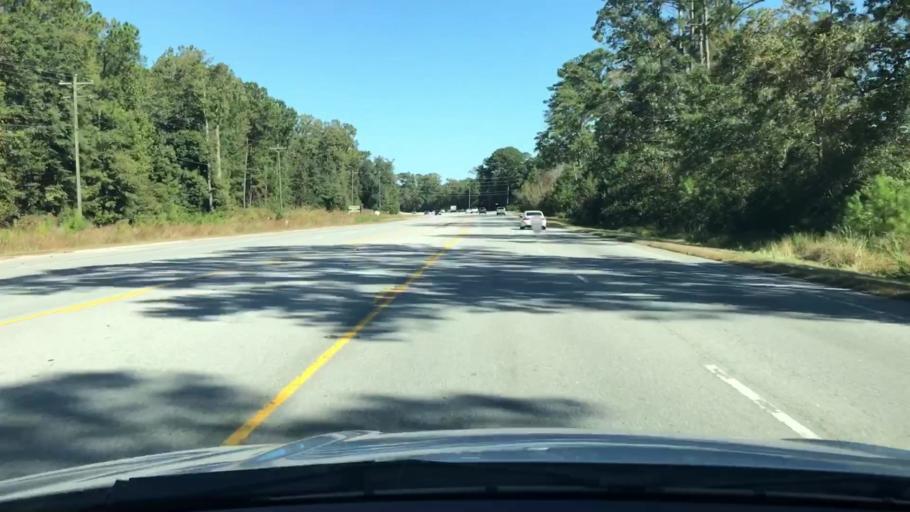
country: US
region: South Carolina
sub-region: Beaufort County
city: Bluffton
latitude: 32.3574
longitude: -80.8790
